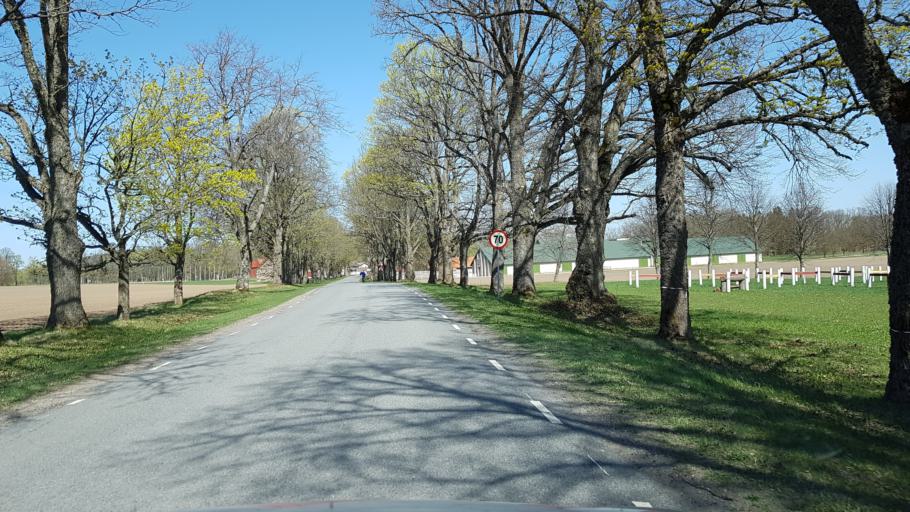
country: EE
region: Viljandimaa
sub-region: Vohma linn
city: Vohma
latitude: 58.5492
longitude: 25.5661
